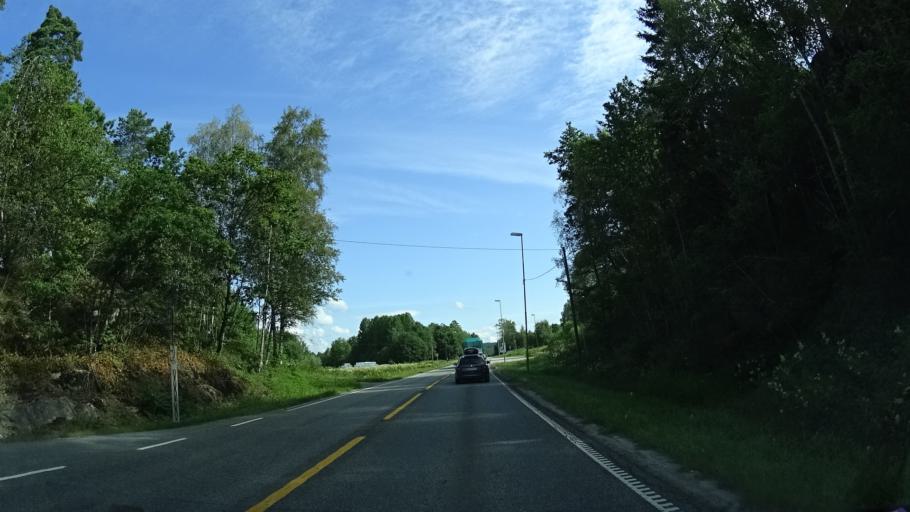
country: NO
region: Telemark
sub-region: Bamble
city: Langesund
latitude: 59.0032
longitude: 9.6549
